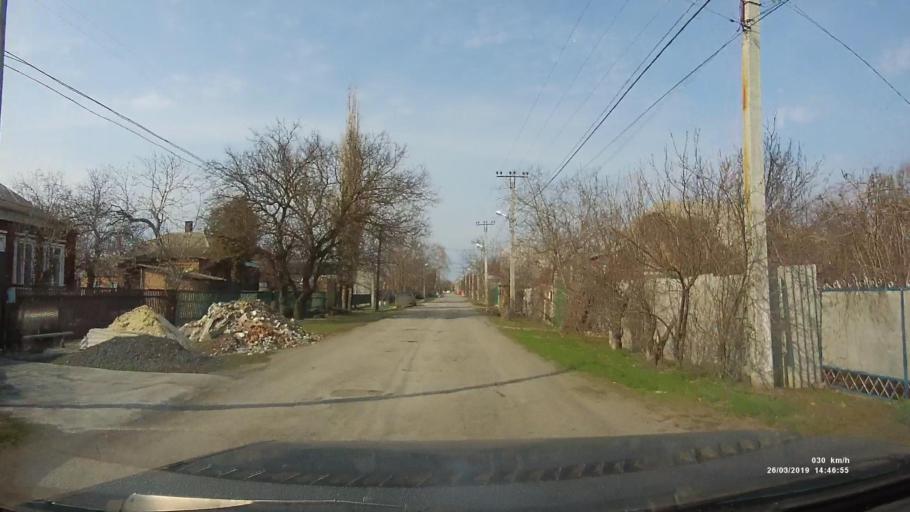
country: RU
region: Rostov
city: Novobessergenovka
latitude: 47.1885
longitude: 38.8597
